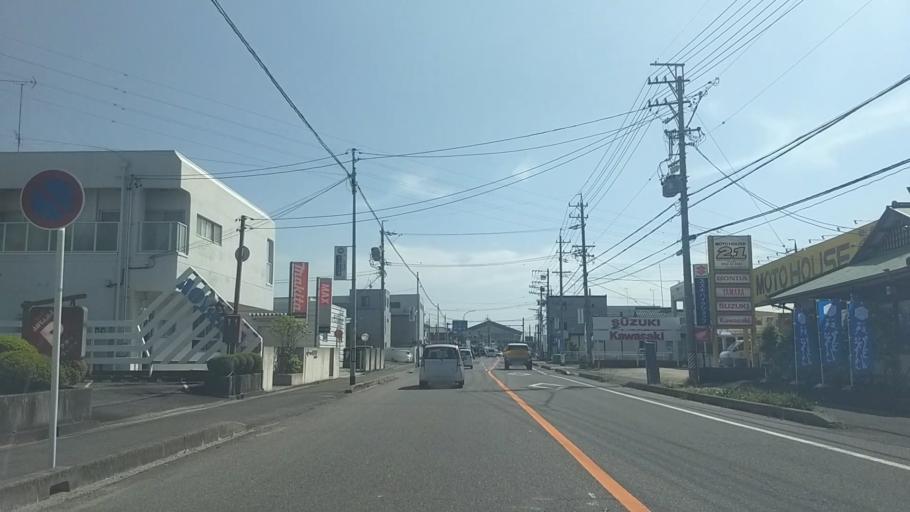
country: JP
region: Aichi
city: Okazaki
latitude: 34.9699
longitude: 137.1317
